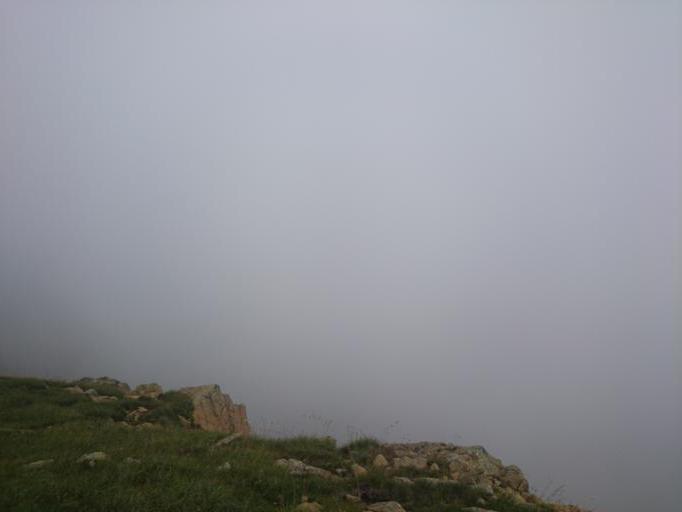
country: AL
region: Diber
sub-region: Rrethi i Dibres
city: Fushe-Lure
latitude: 41.7854
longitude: 20.1816
